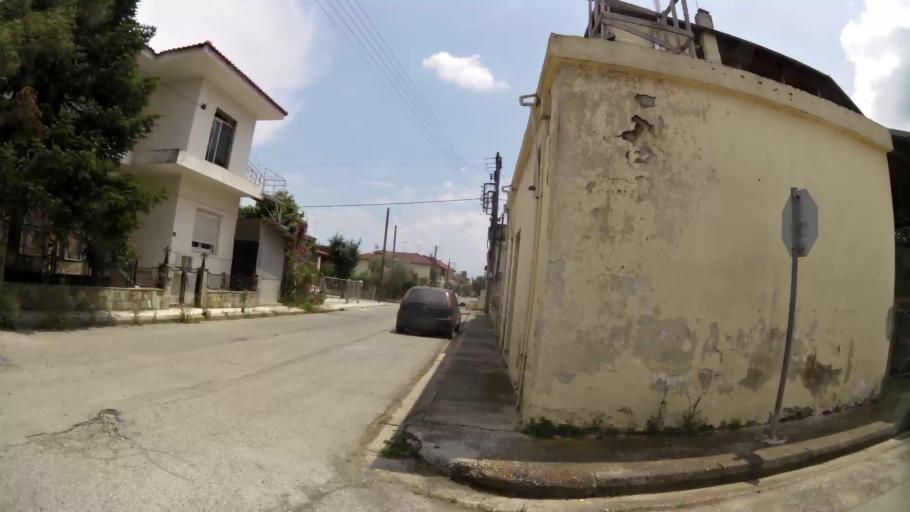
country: GR
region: Central Macedonia
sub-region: Nomos Pierias
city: Peristasi
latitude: 40.2764
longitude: 22.5425
